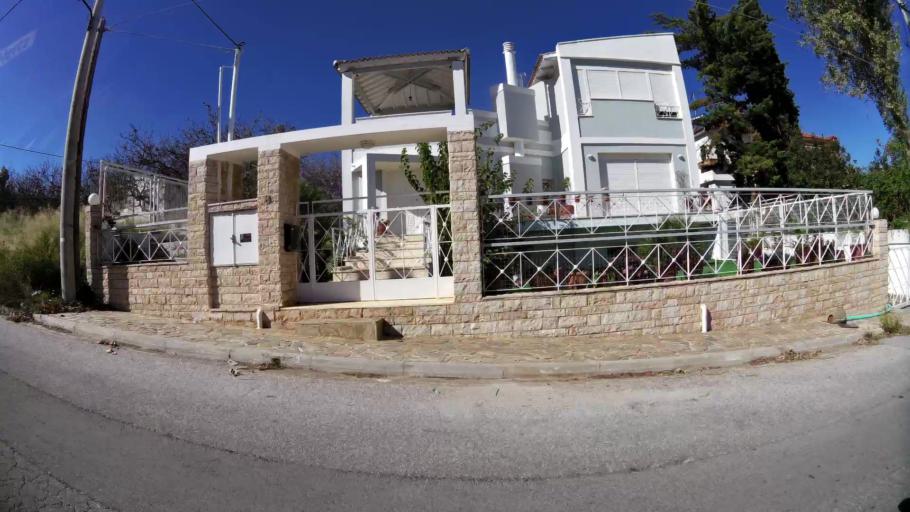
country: GR
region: Attica
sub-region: Nomarchia Anatolikis Attikis
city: Markopoulo
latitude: 37.8864
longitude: 23.9425
